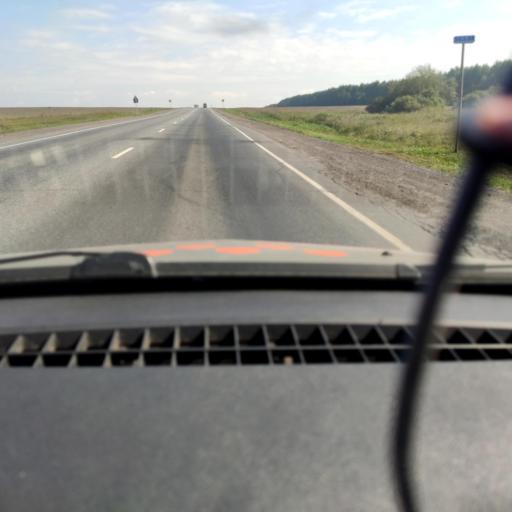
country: RU
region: Bashkortostan
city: Iglino
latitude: 54.7559
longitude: 56.3644
